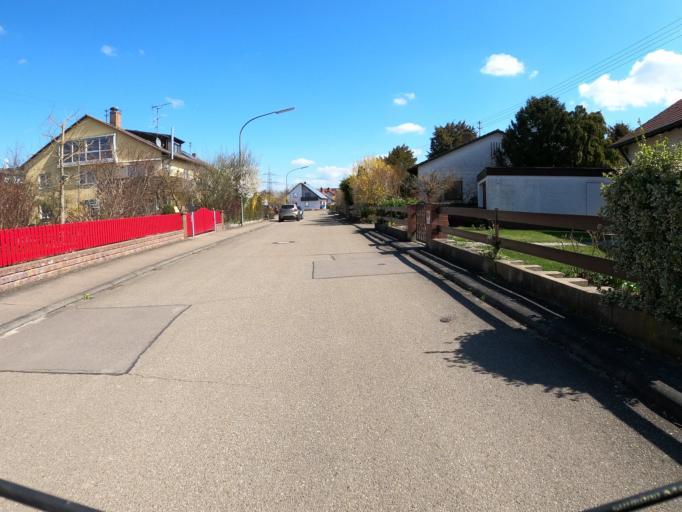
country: DE
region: Bavaria
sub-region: Swabia
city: Nersingen
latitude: 48.4266
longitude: 10.1277
